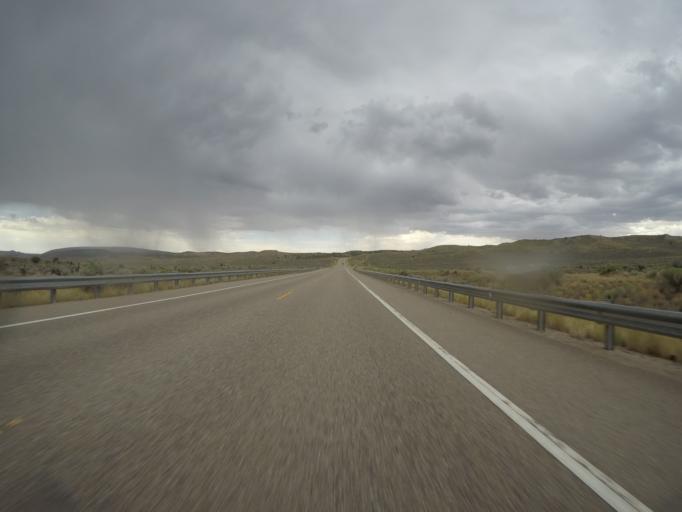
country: US
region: Colorado
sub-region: Rio Blanco County
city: Rangely
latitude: 40.4010
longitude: -108.3436
